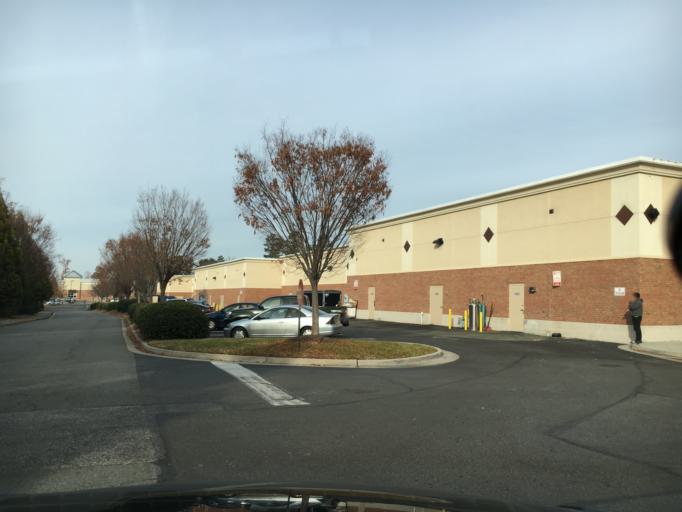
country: US
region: Virginia
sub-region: Henrico County
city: Short Pump
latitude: 37.6515
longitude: -77.6171
